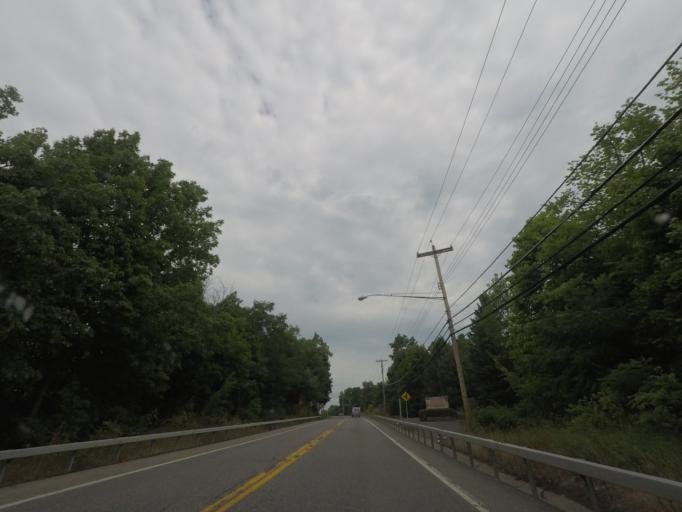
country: US
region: New York
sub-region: Saratoga County
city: Waterford
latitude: 42.7959
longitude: -73.6798
